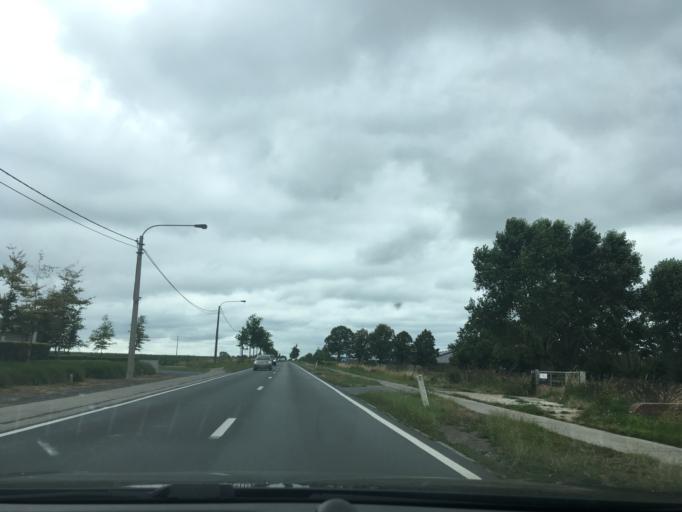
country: BE
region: Flanders
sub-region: Provincie West-Vlaanderen
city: Tielt
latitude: 51.0174
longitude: 3.3099
